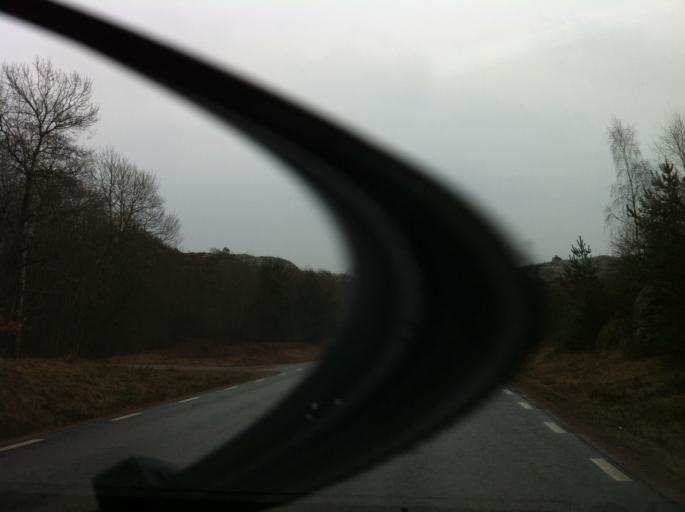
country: SE
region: Vaestra Goetaland
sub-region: Sotenas Kommun
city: Kungshamn
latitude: 58.3969
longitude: 11.2649
